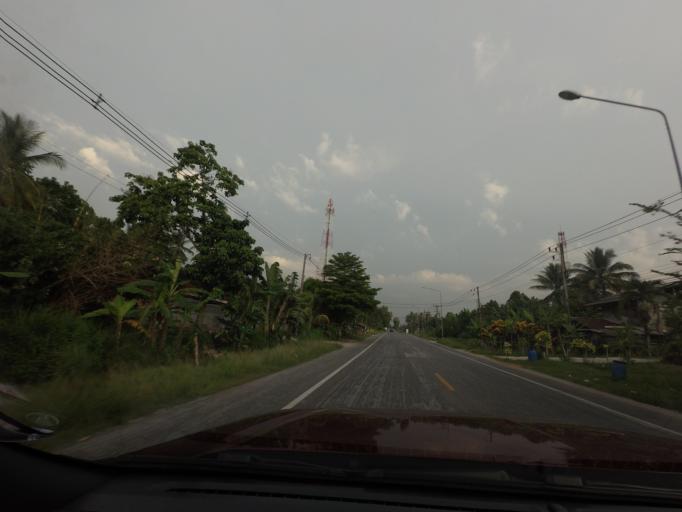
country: TH
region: Pattani
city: Mae Lan
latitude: 6.5888
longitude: 101.1963
